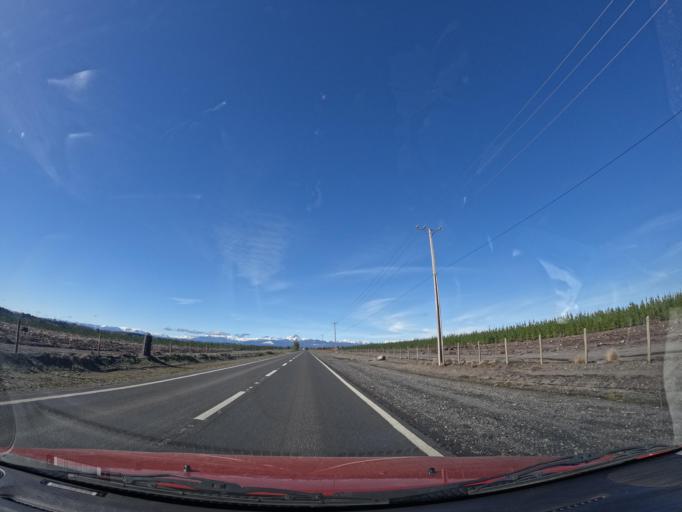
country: CL
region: Biobio
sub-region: Provincia de Biobio
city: Los Angeles
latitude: -37.4140
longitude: -72.0124
